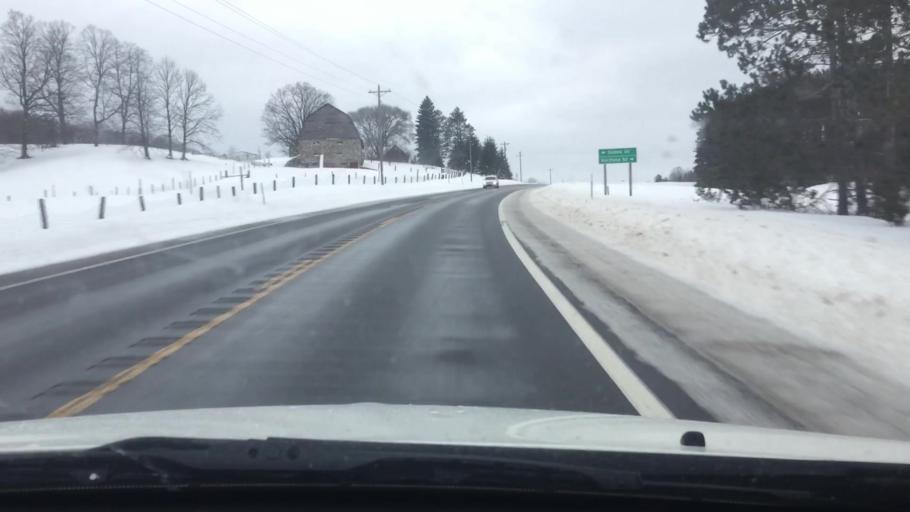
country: US
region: Michigan
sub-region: Charlevoix County
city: Boyne City
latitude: 45.0947
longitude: -84.9757
